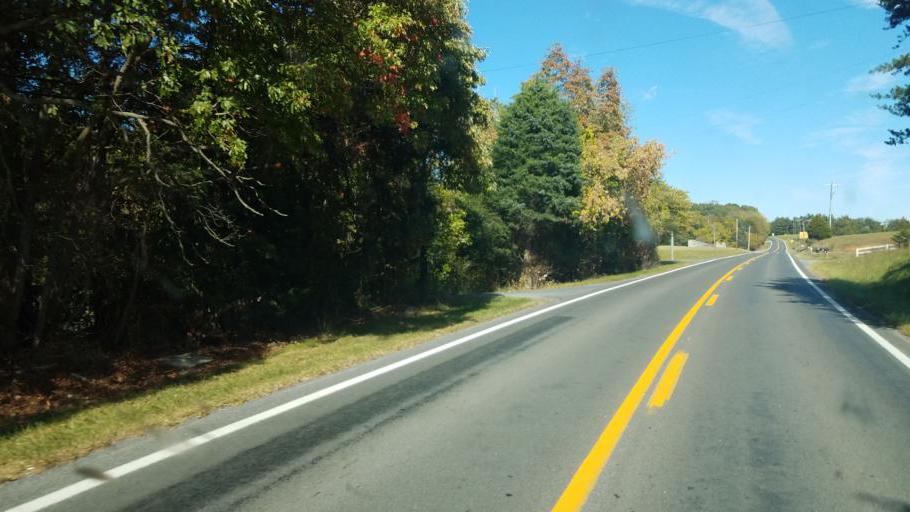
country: US
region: Virginia
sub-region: Warren County
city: Front Royal
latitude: 38.8939
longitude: -78.2381
